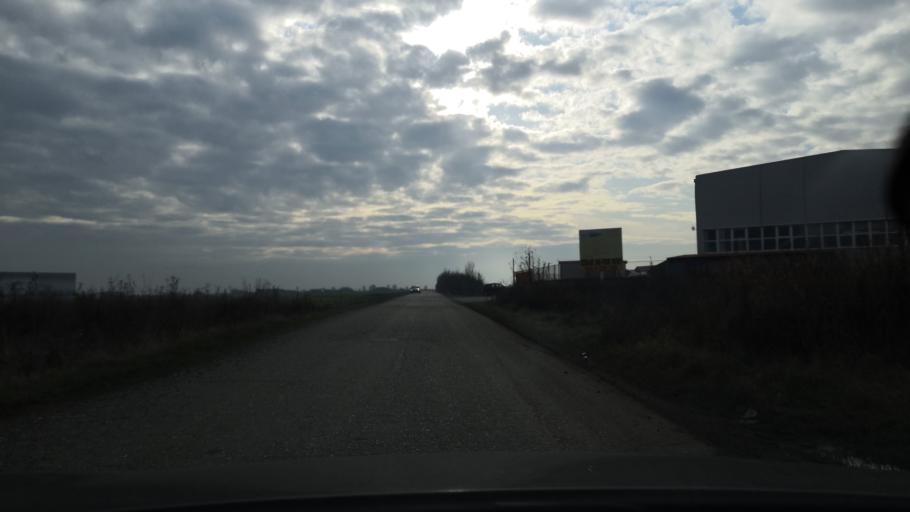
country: RS
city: Ugrinovci
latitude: 44.8847
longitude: 20.1481
